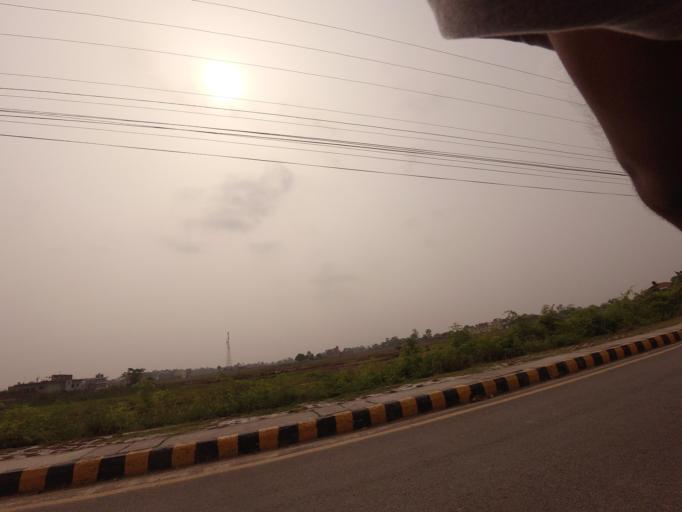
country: IN
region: Uttar Pradesh
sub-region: Maharajganj
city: Nautanwa
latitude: 27.4885
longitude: 83.2844
